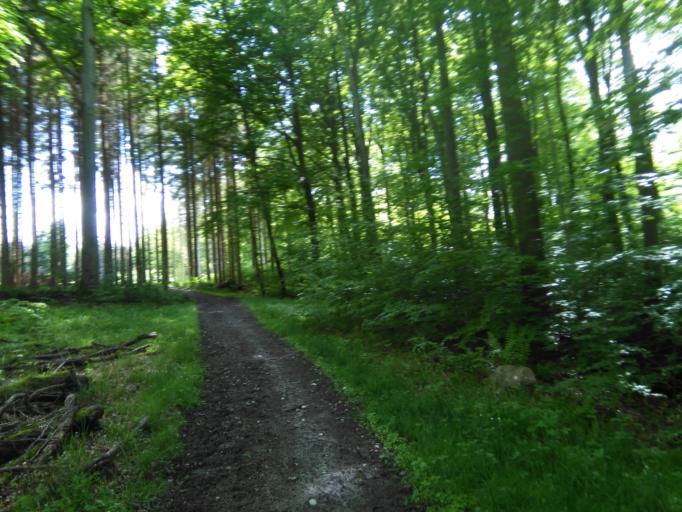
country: DK
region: Central Jutland
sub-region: Arhus Kommune
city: Beder
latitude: 56.0703
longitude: 10.2489
